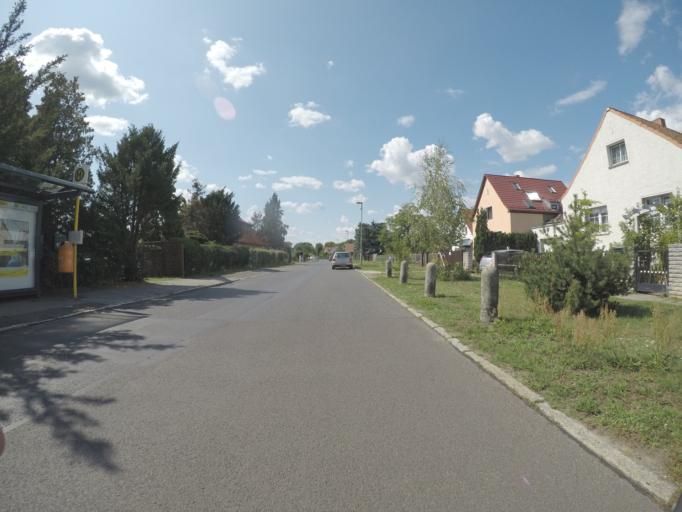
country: DE
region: Berlin
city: Mahlsdorf
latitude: 52.5105
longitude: 13.6018
